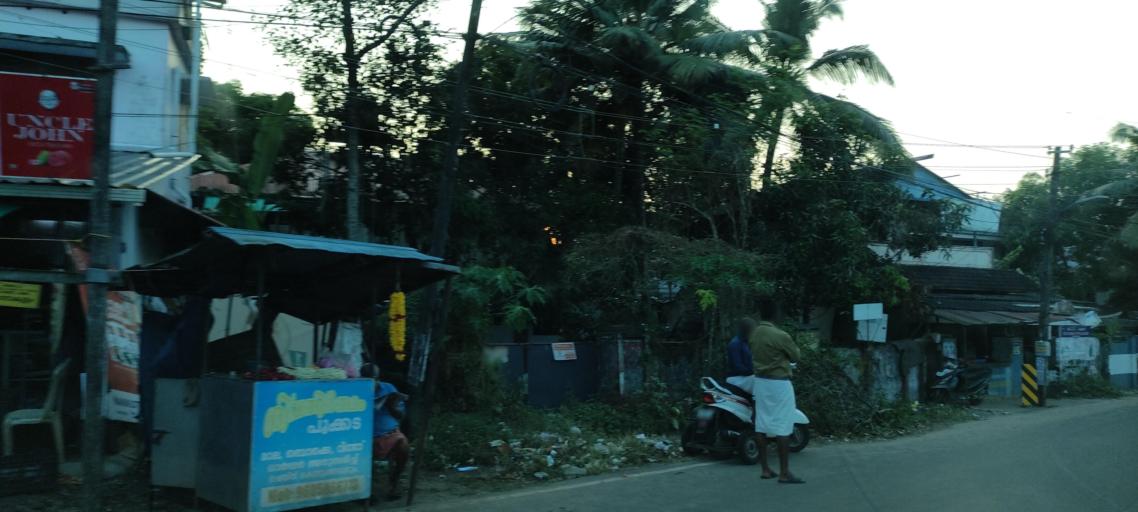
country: IN
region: Kerala
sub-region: Alappuzha
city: Alleppey
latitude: 9.4667
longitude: 76.3421
